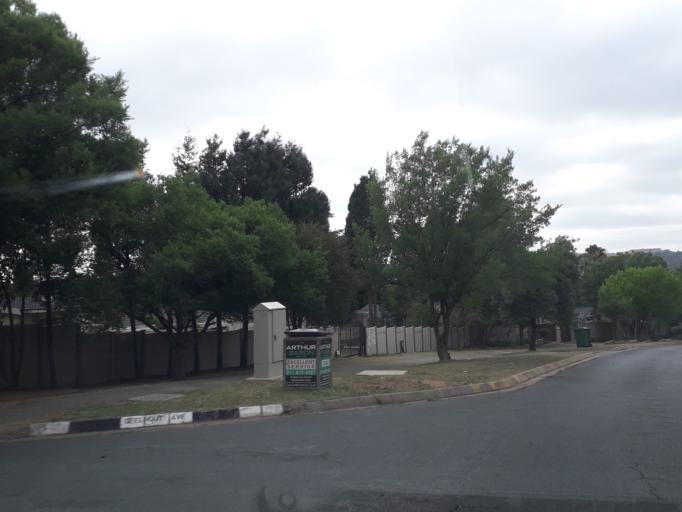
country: ZA
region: Gauteng
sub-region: City of Johannesburg Metropolitan Municipality
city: Roodepoort
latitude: -26.0987
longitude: 27.9599
